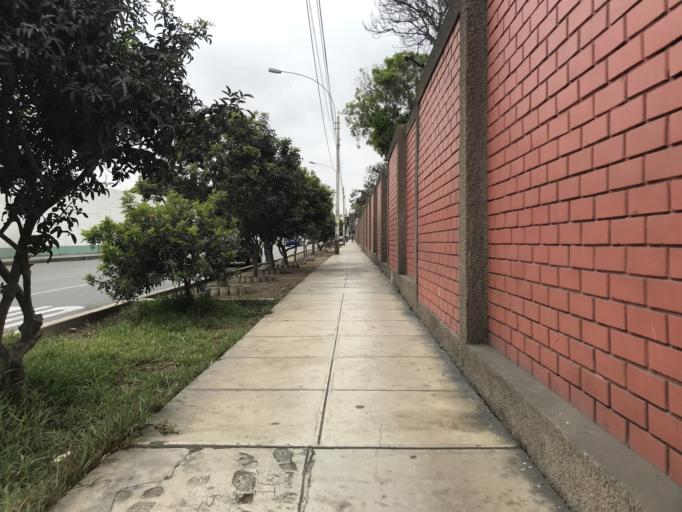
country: PE
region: Callao
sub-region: Callao
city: Callao
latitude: -12.0732
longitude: -77.0759
